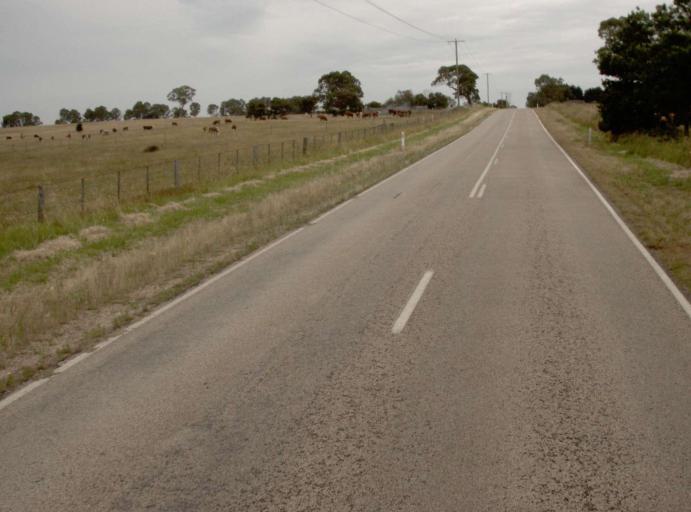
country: AU
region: Victoria
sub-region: East Gippsland
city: Bairnsdale
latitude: -37.8111
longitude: 147.4374
